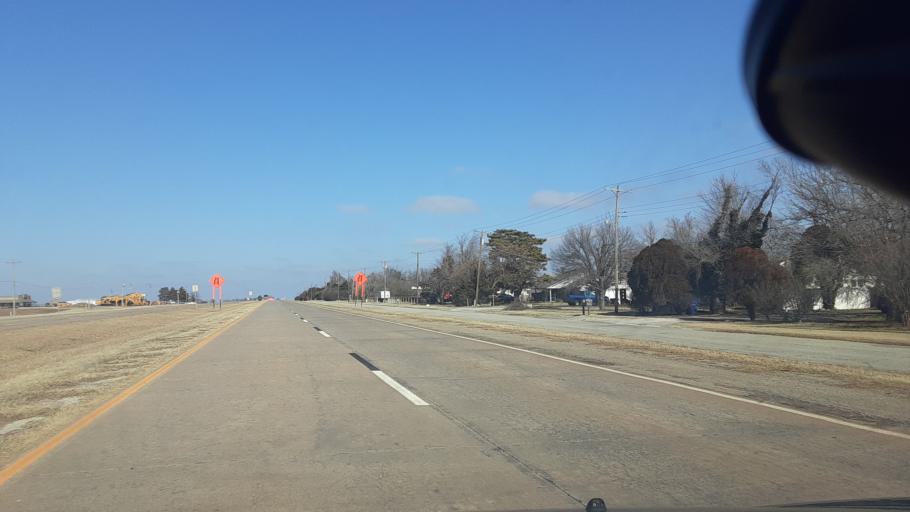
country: US
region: Oklahoma
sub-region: Garfield County
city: Enid
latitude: 36.4516
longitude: -97.8729
